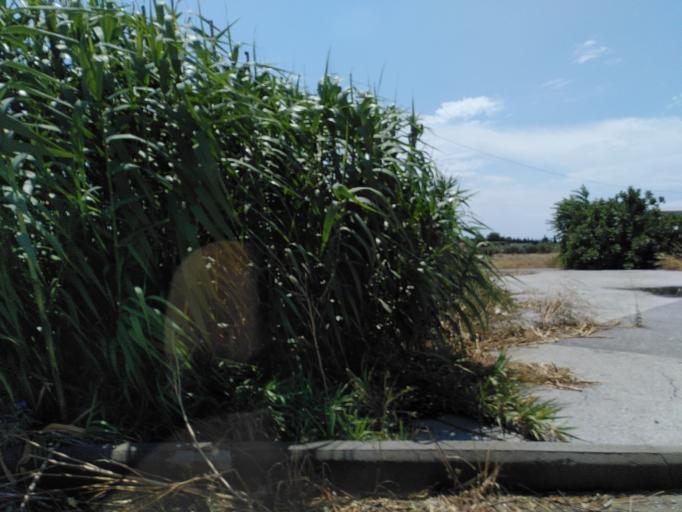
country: GR
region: Central Macedonia
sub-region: Nomos Thessalonikis
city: Agia Triada
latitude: 40.4925
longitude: 22.8583
